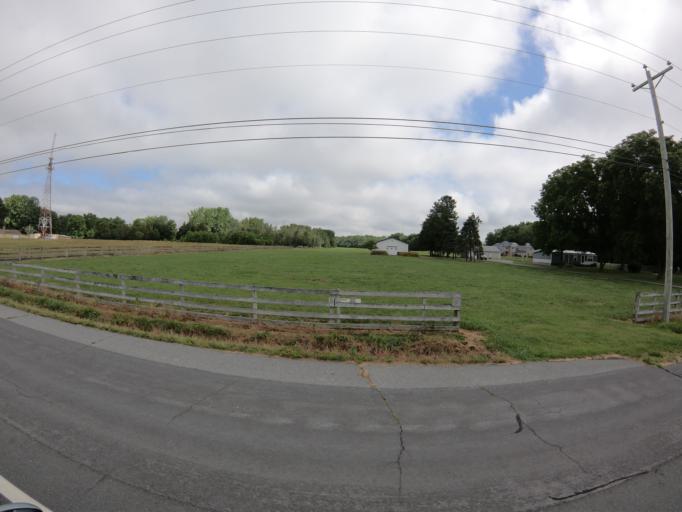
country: US
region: Delaware
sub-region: Kent County
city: Riverview
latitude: 39.0114
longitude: -75.5057
